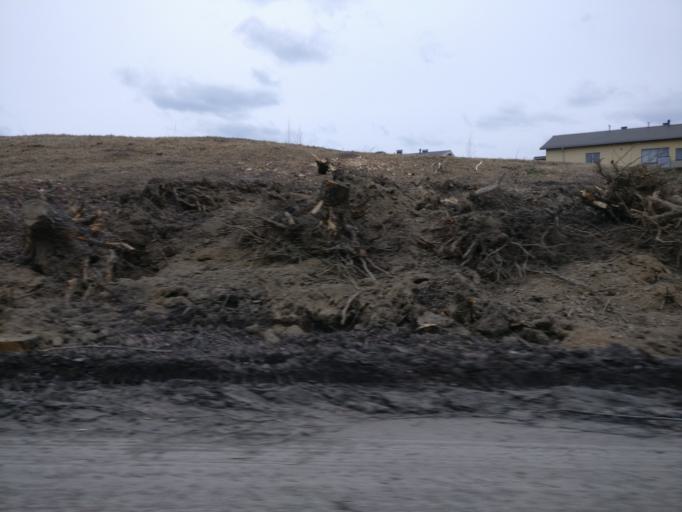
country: FI
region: Pirkanmaa
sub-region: Tampere
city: Tampere
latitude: 61.4758
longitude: 23.8353
